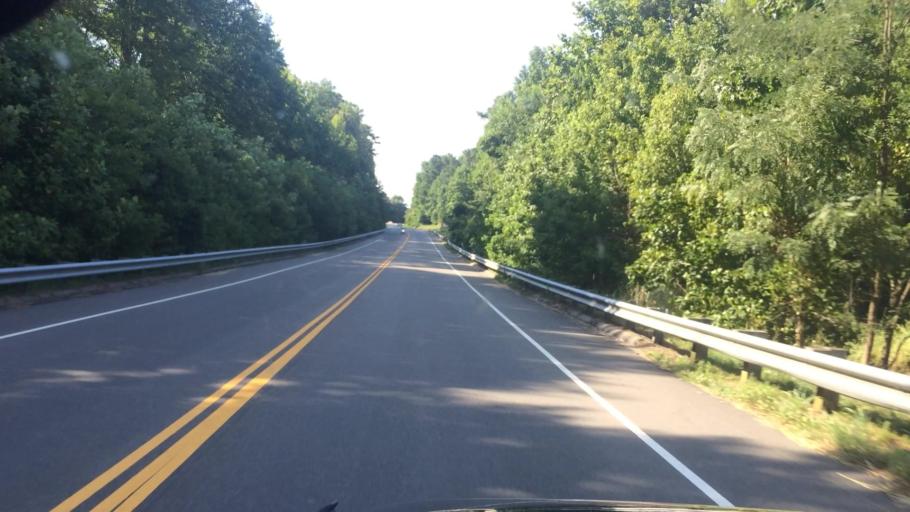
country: US
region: Virginia
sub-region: James City County
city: Williamsburg
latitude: 37.2975
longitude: -76.7246
